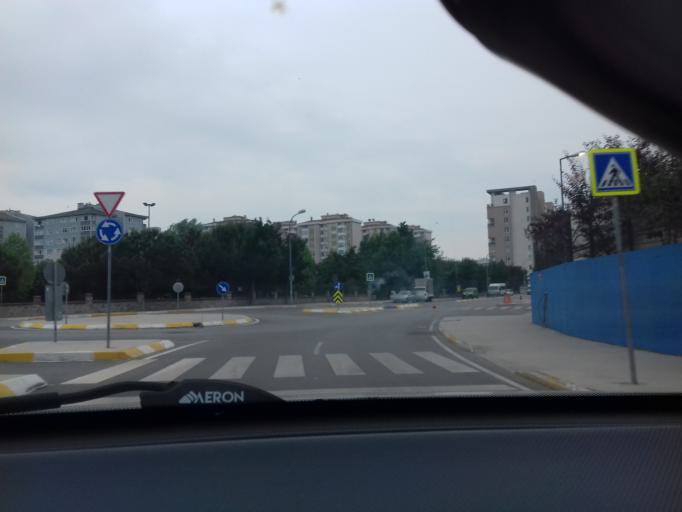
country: TR
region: Istanbul
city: Sultanbeyli
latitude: 40.9249
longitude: 29.2928
